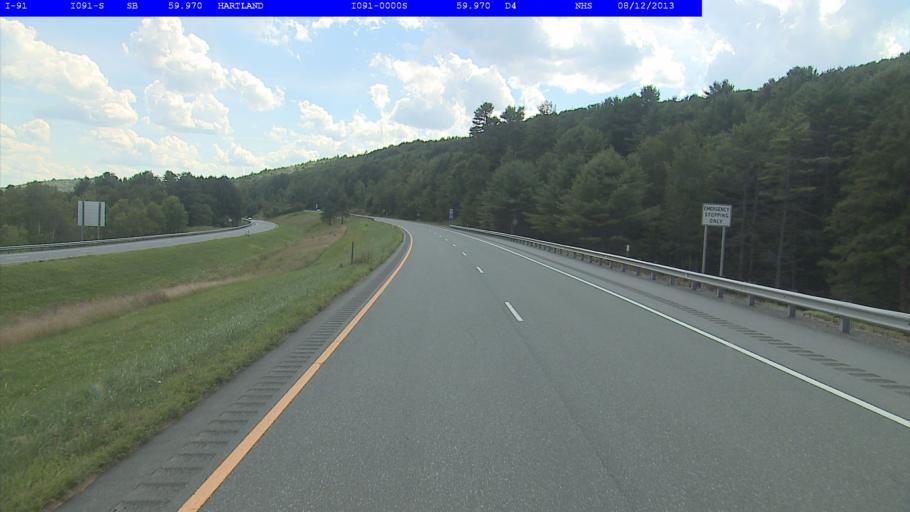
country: US
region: Vermont
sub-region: Windsor County
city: Windsor
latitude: 43.5225
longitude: -72.4083
